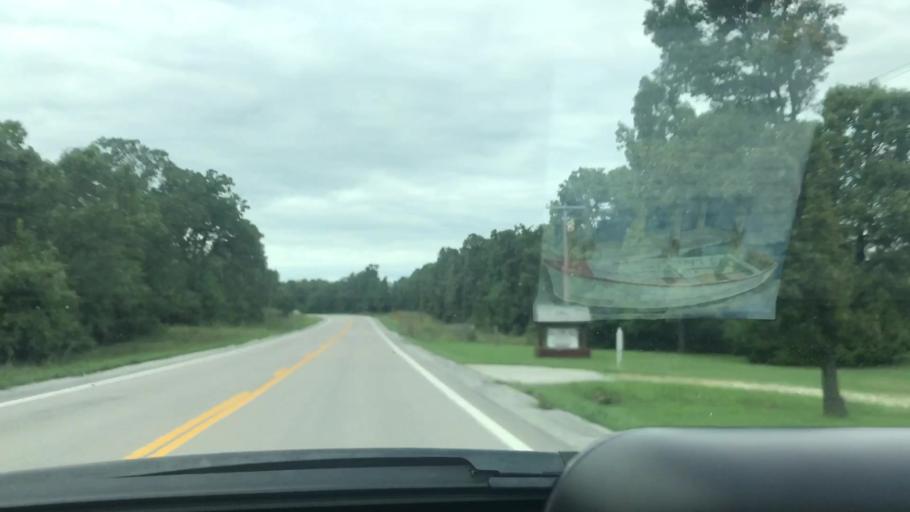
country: US
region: Missouri
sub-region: Benton County
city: Warsaw
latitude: 38.1570
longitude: -93.2970
